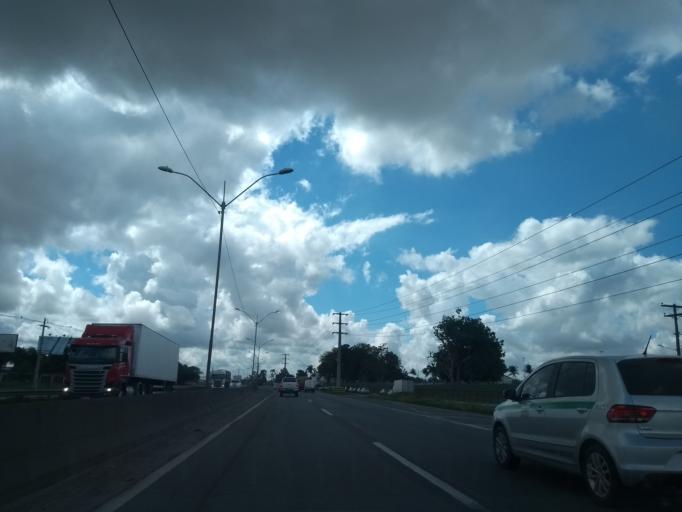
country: BR
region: Bahia
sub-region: Feira De Santana
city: Feira de Santana
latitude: -12.2801
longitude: -38.9425
